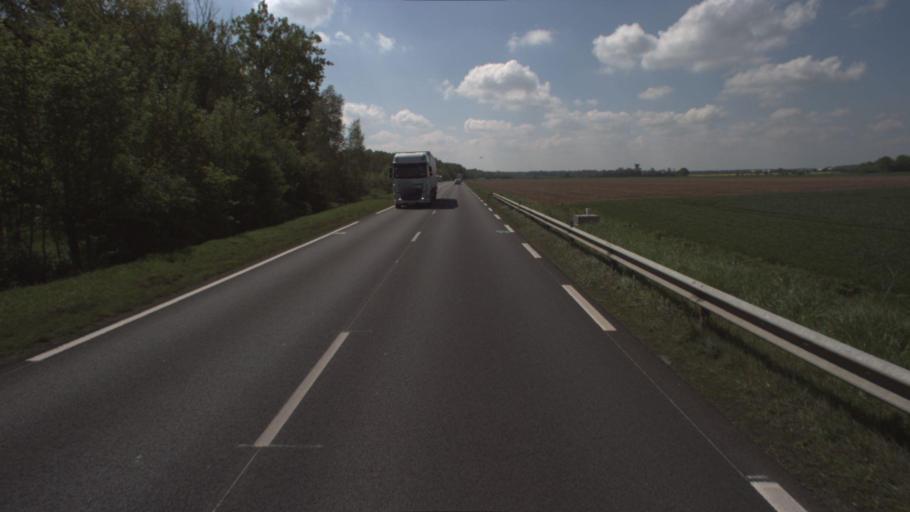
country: FR
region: Ile-de-France
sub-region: Departement de Seine-et-Marne
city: La Houssaye-en-Brie
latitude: 48.7441
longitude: 2.8574
